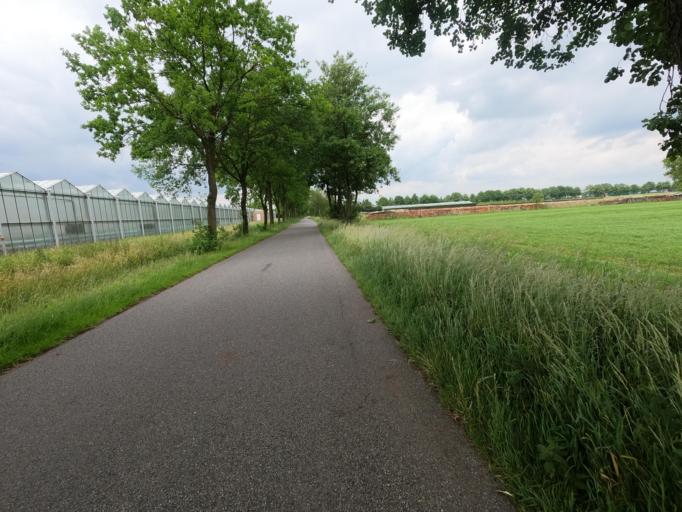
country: BE
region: Flanders
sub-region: Provincie Antwerpen
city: Kalmthout
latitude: 51.3882
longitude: 4.4893
